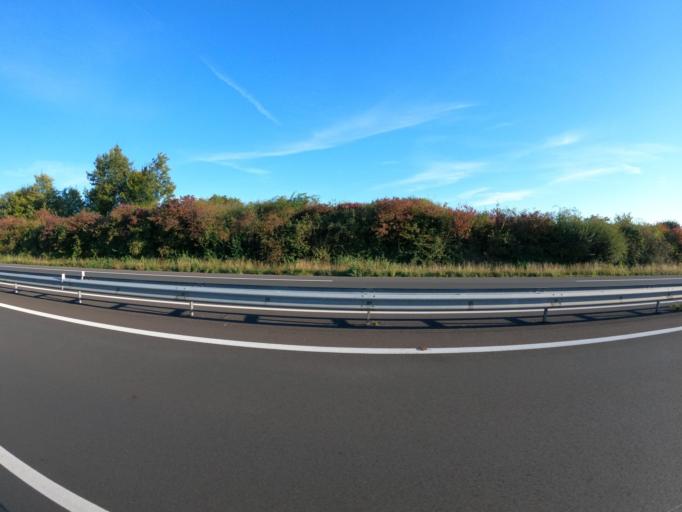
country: FR
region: Pays de la Loire
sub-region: Departement de la Vendee
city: Beaurepaire
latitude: 46.8936
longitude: -1.0908
